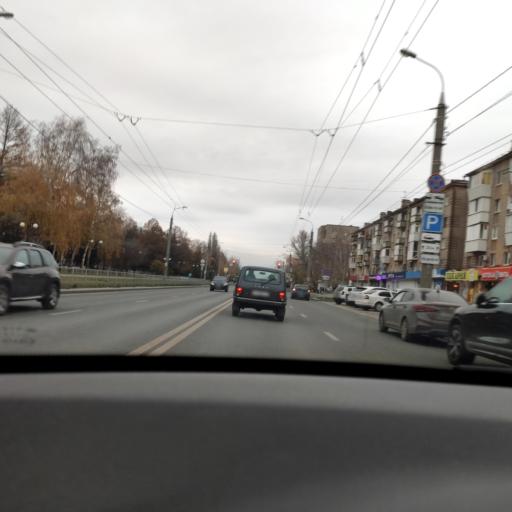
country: RU
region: Samara
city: Samara
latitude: 53.2308
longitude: 50.2114
